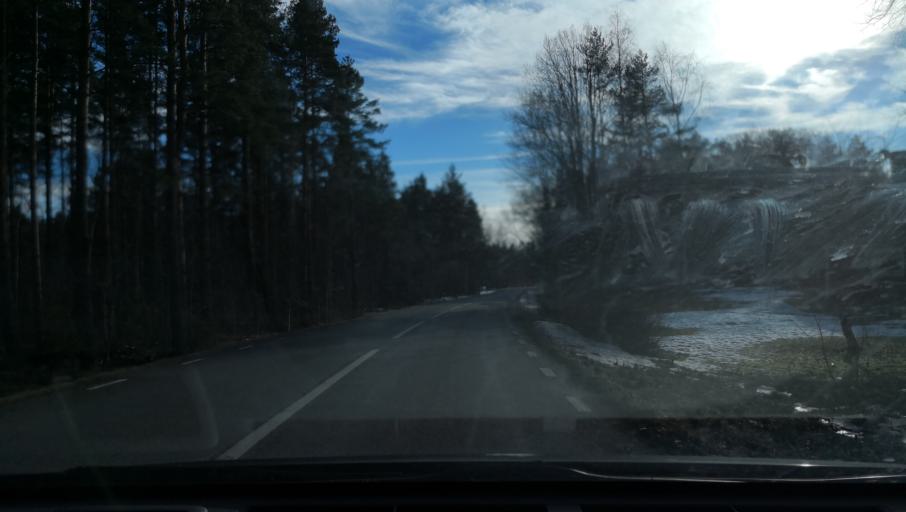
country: SE
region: Uppsala
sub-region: Osthammars Kommun
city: Osterbybruk
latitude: 60.2718
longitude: 17.9578
